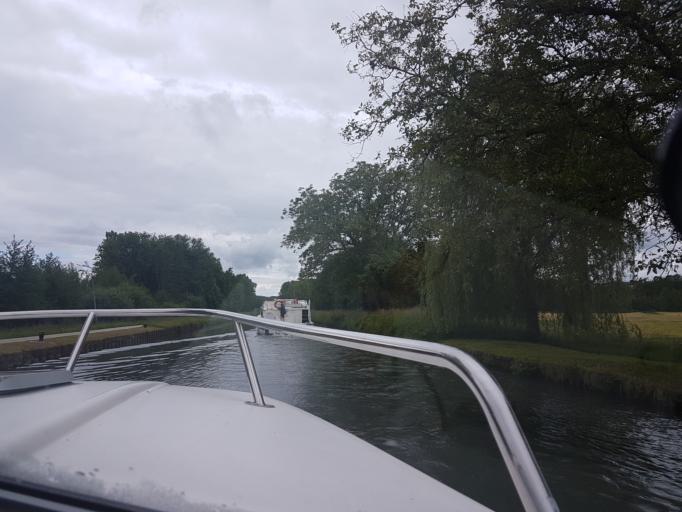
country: FR
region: Bourgogne
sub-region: Departement de l'Yonne
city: Vermenton
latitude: 47.6537
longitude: 3.6712
